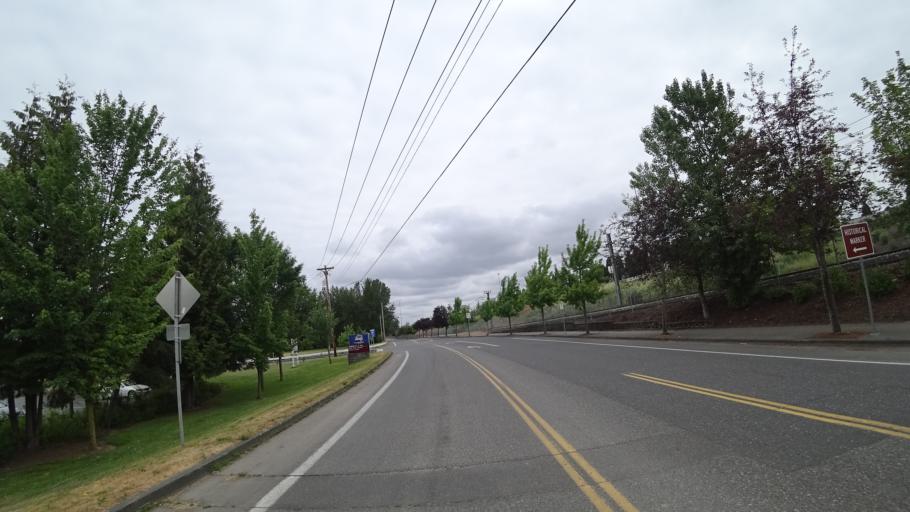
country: US
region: Washington
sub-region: Clark County
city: Vancouver
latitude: 45.5972
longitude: -122.6856
